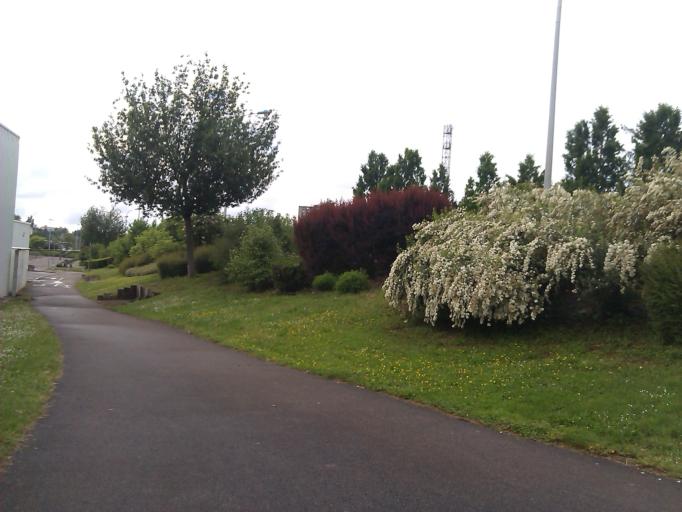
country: FR
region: Bourgogne
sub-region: Departement de Saone-et-Loire
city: Chalon-sur-Saone
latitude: 46.7857
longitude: 4.8678
